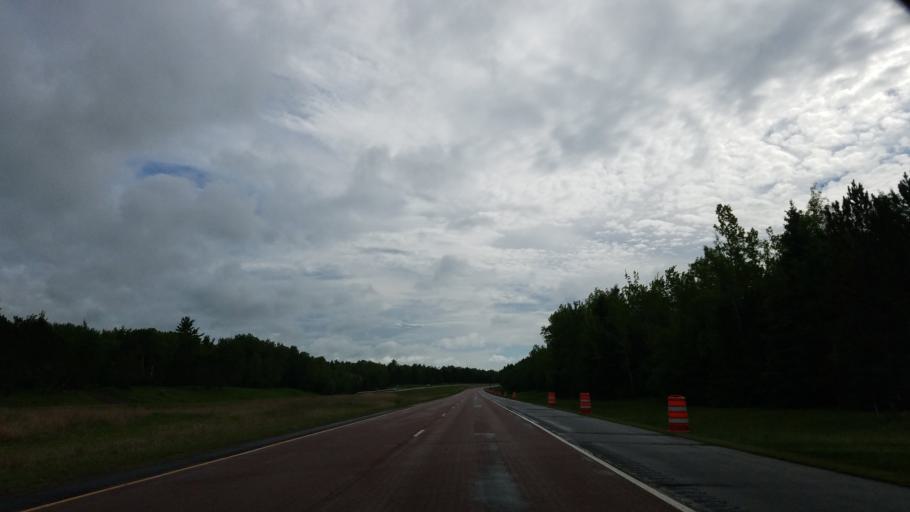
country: US
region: Minnesota
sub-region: Lake County
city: Two Harbors
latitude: 46.9240
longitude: -91.8587
